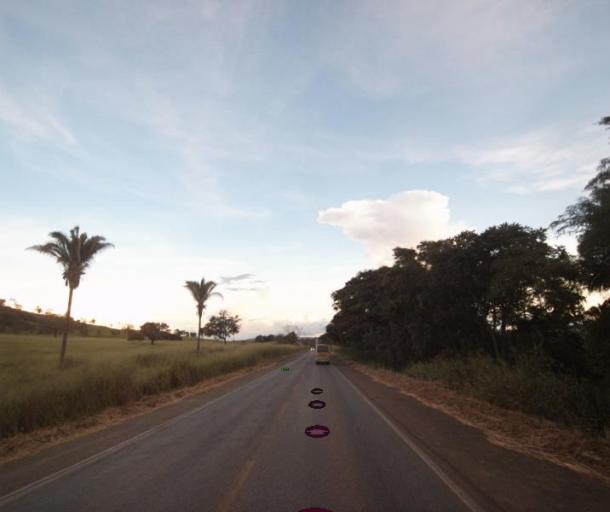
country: BR
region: Goias
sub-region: Uruacu
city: Uruacu
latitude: -14.4054
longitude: -49.1575
